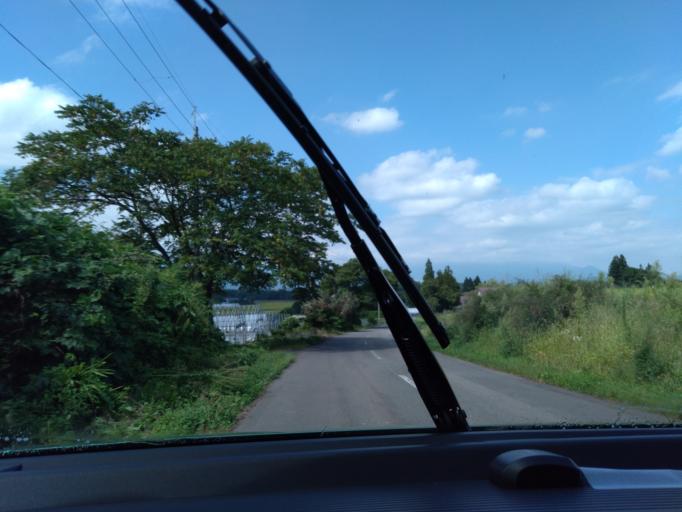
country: JP
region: Iwate
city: Shizukuishi
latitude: 39.6801
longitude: 140.9591
